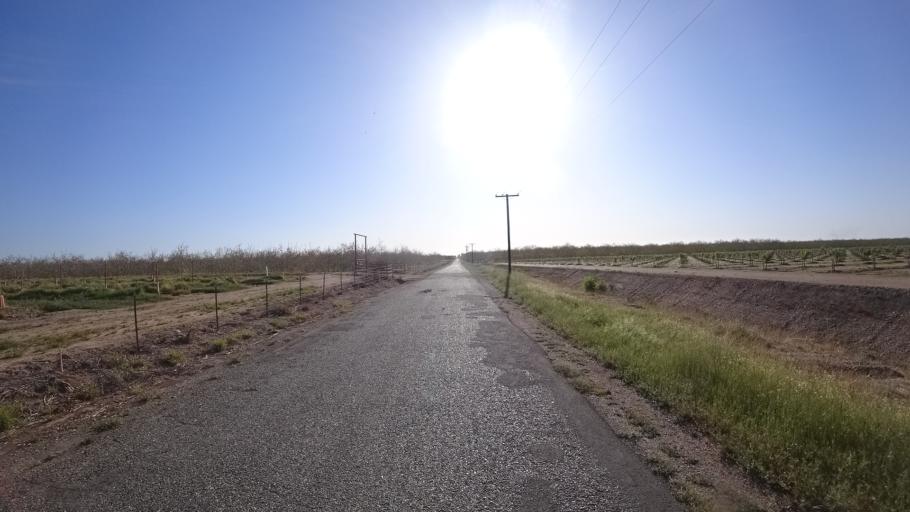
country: US
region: California
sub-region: Glenn County
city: Orland
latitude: 39.6821
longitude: -122.1729
